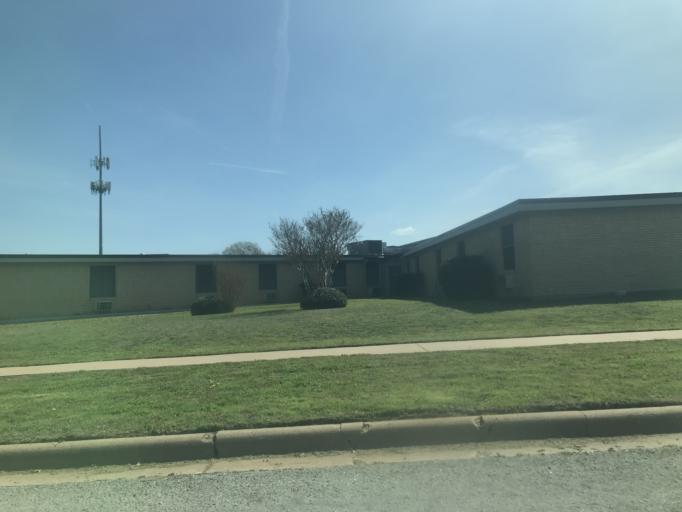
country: US
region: Texas
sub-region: Taylor County
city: Abilene
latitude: 32.4661
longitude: -99.7424
